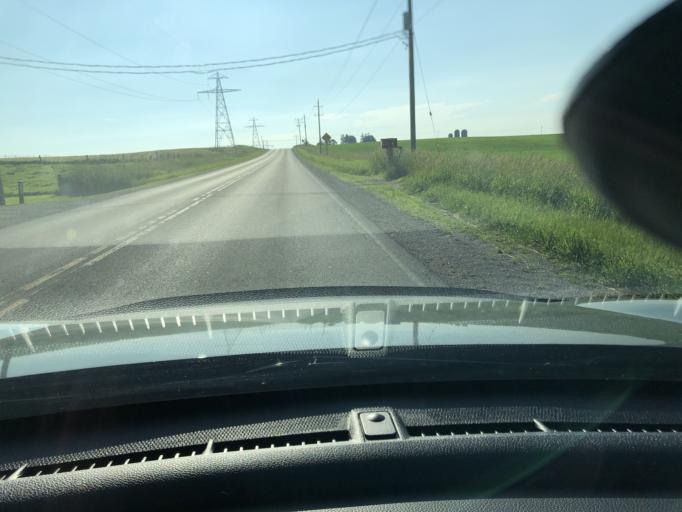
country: CA
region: Ontario
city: Stratford
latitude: 43.3886
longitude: -80.9167
